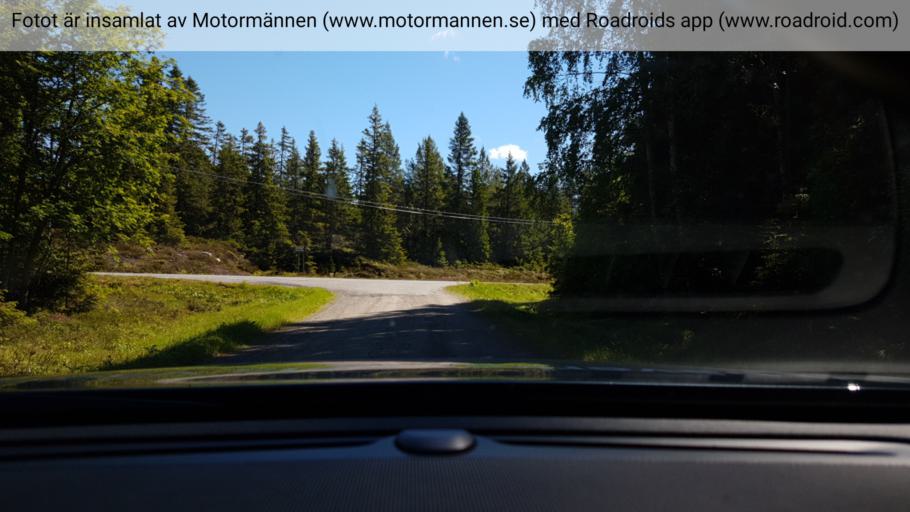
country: SE
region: Vaesterbotten
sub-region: Skelleftea Kommun
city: Skelleftehamn
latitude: 64.4696
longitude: 21.5825
